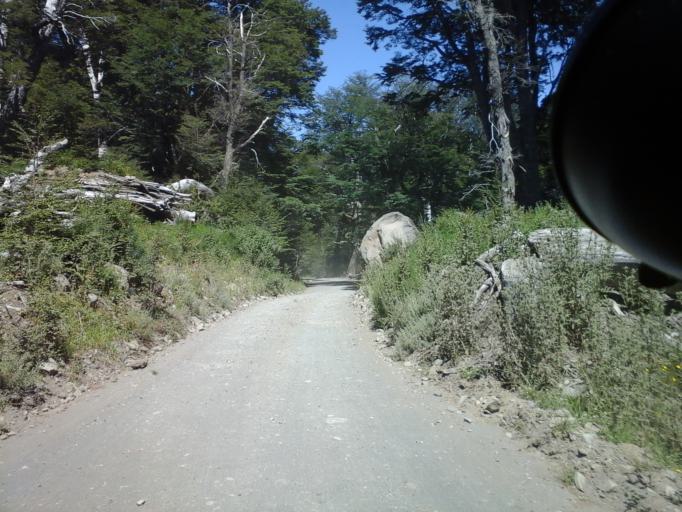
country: AR
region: Neuquen
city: Villa La Angostura
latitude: -41.2110
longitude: -71.8091
